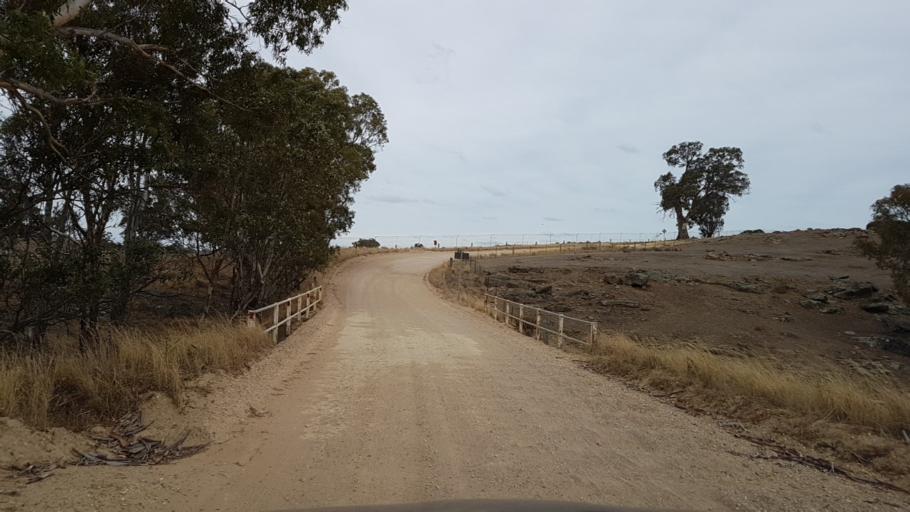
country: AU
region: South Australia
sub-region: Adelaide Hills
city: Birdwood
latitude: -34.8688
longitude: 139.0776
